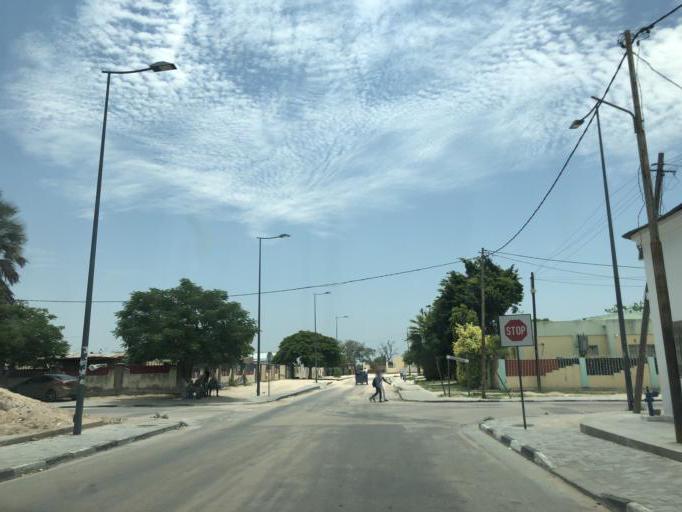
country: AO
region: Cunene
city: Ondjiva
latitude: -17.0676
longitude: 15.7217
